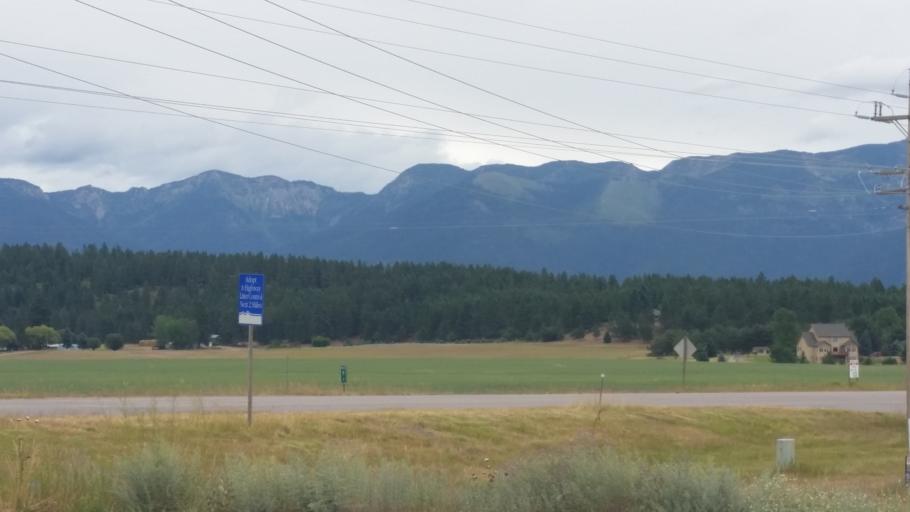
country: US
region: Montana
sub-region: Flathead County
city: Bigfork
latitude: 48.0952
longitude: -114.0875
